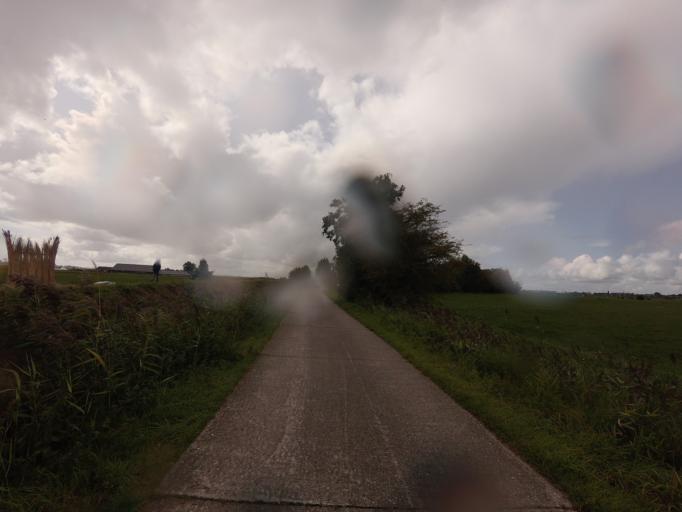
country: NL
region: Friesland
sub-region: Gemeente Boarnsterhim
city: Wergea
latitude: 53.1476
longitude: 5.8268
